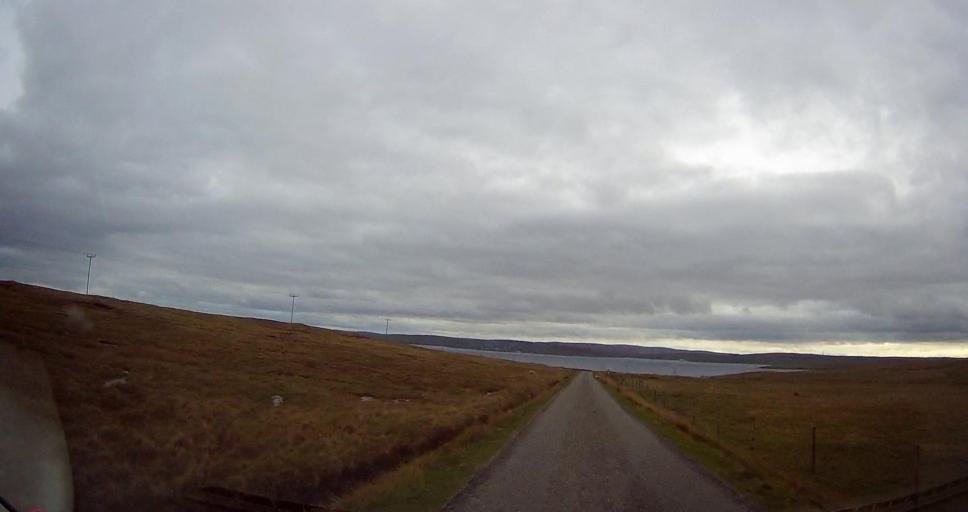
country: GB
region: Scotland
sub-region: Shetland Islands
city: Shetland
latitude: 60.5043
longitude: -1.1469
